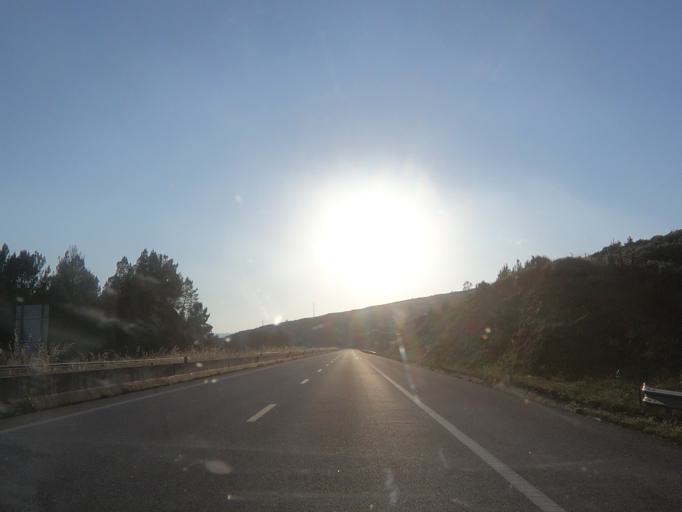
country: PT
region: Guarda
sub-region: Celorico da Beira
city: Celorico da Beira
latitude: 40.6333
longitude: -7.4400
